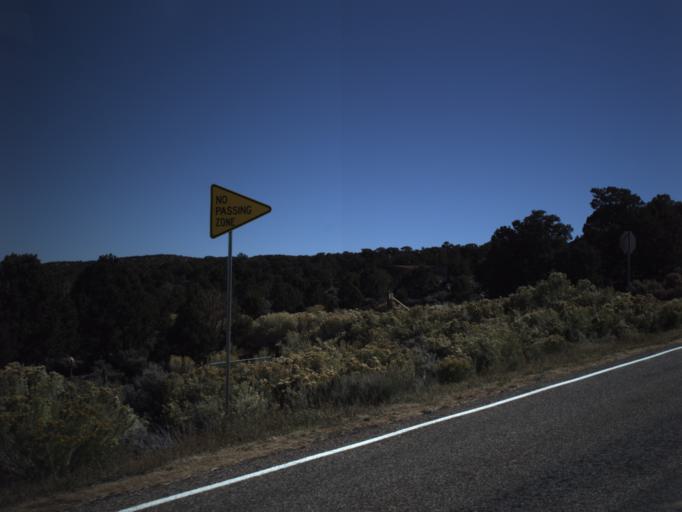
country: US
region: Utah
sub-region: Wayne County
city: Loa
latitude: 38.2318
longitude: -111.3617
